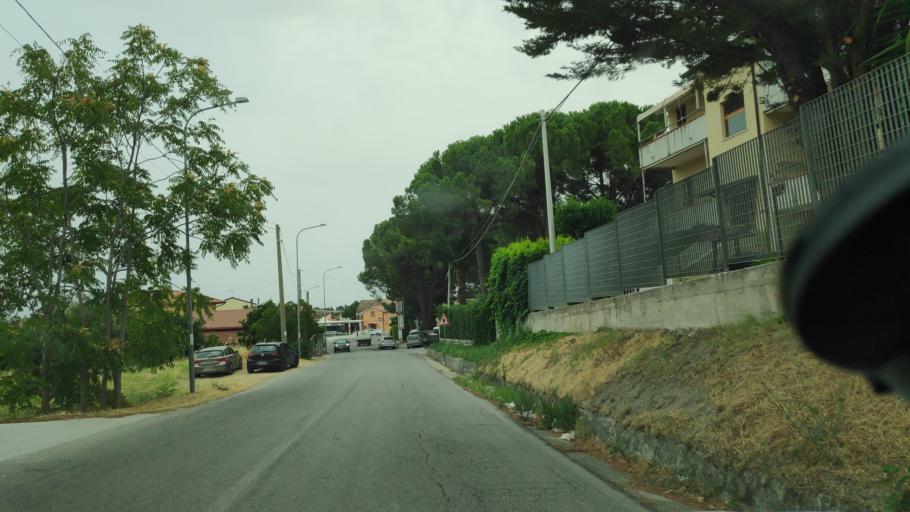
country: IT
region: Calabria
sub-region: Provincia di Catanzaro
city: Martelli-Laganosa
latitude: 38.6671
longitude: 16.5235
